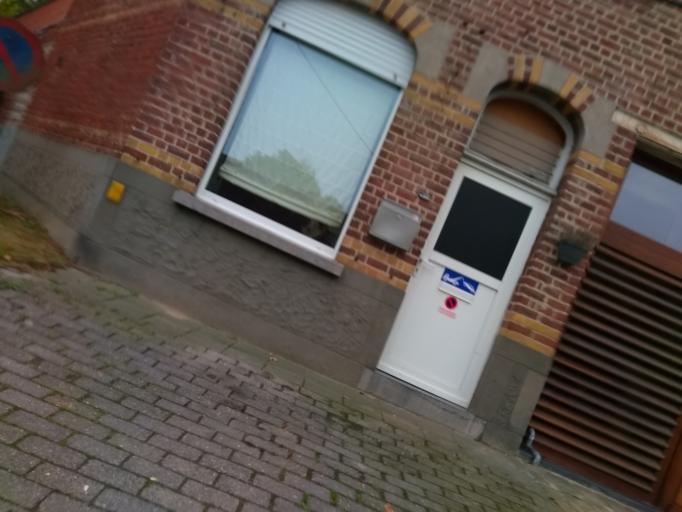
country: BE
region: Flanders
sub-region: Provincie Oost-Vlaanderen
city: Oosterzele
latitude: 50.9363
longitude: 3.7760
